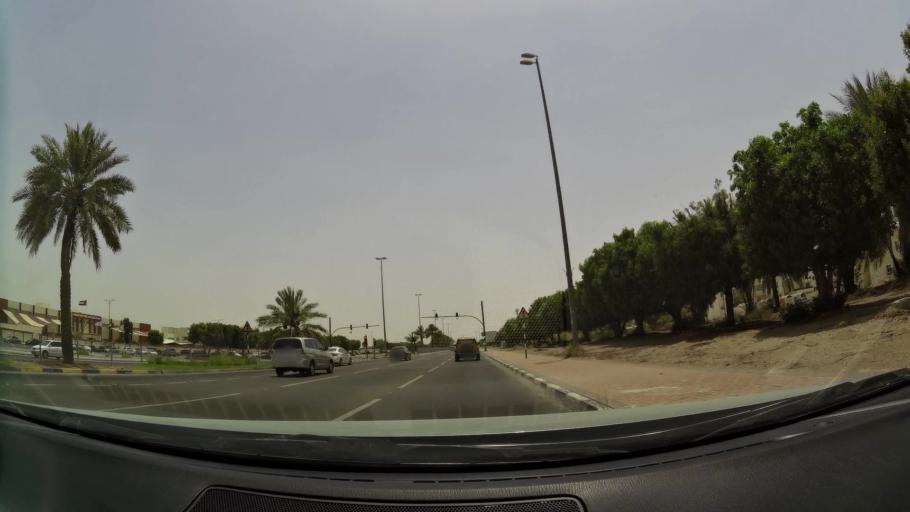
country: AE
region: Abu Dhabi
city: Al Ain
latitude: 24.2027
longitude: 55.7192
